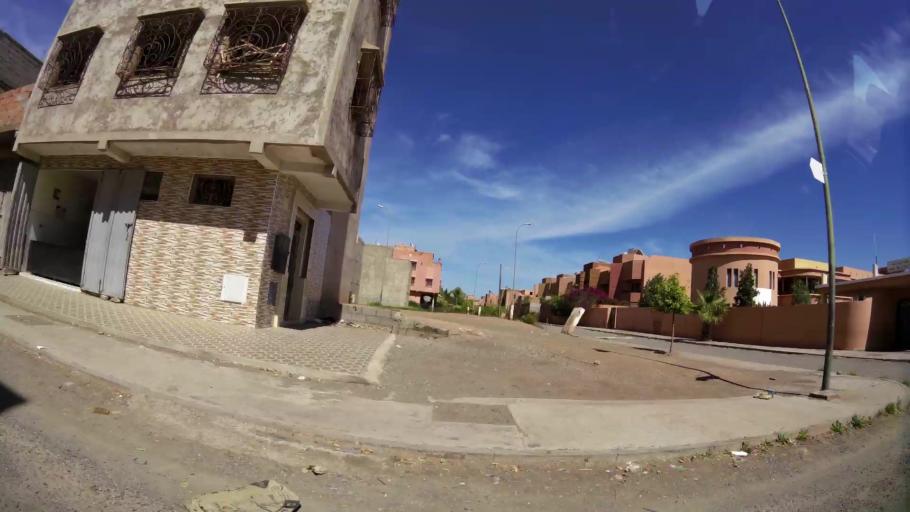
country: MA
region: Marrakech-Tensift-Al Haouz
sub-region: Marrakech
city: Marrakesh
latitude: 31.6374
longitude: -8.1091
